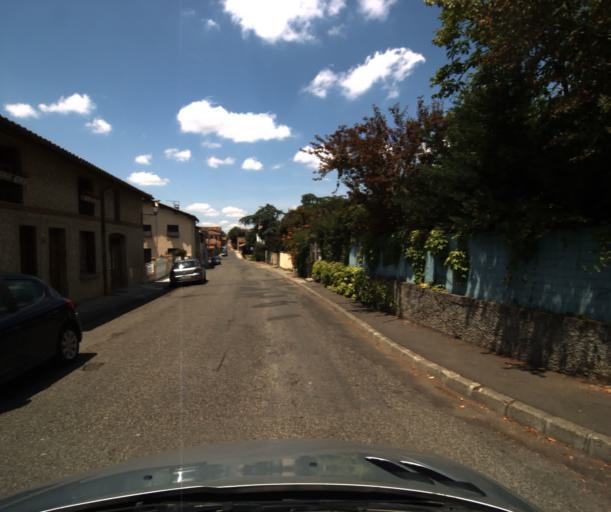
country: FR
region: Midi-Pyrenees
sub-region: Departement de la Haute-Garonne
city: Saint-Lys
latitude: 43.5119
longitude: 1.1782
